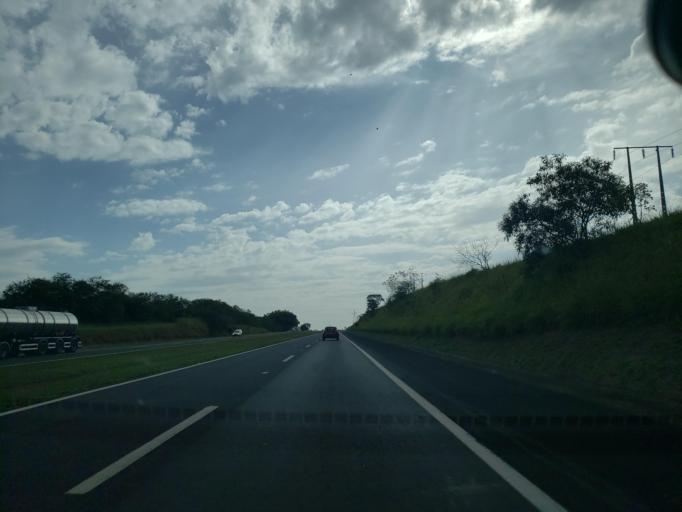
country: BR
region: Sao Paulo
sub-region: Lins
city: Lins
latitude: -21.7399
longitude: -49.6997
